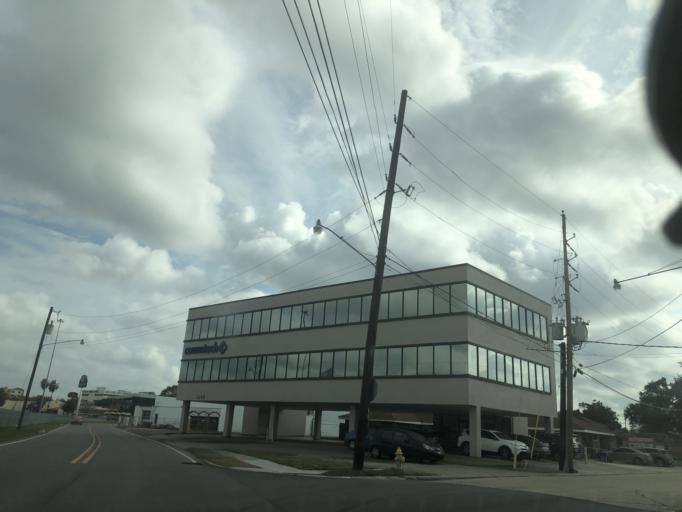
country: US
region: Louisiana
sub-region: Jefferson Parish
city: Metairie
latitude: 29.9959
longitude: -90.1576
